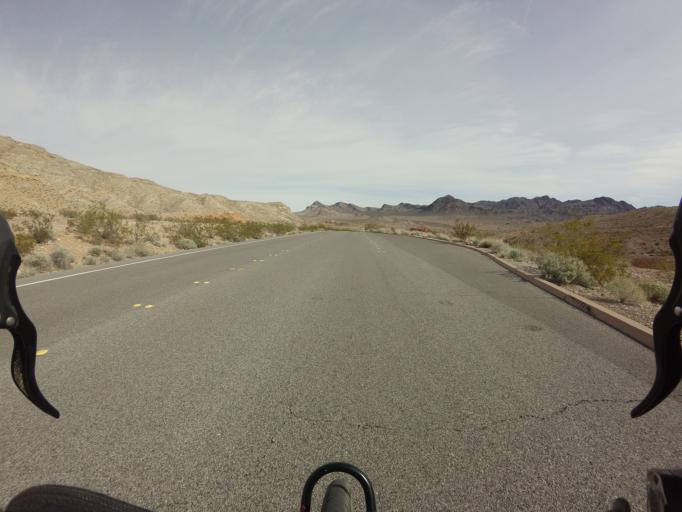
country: US
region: Nevada
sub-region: Clark County
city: Boulder City
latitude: 36.1963
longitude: -114.7035
